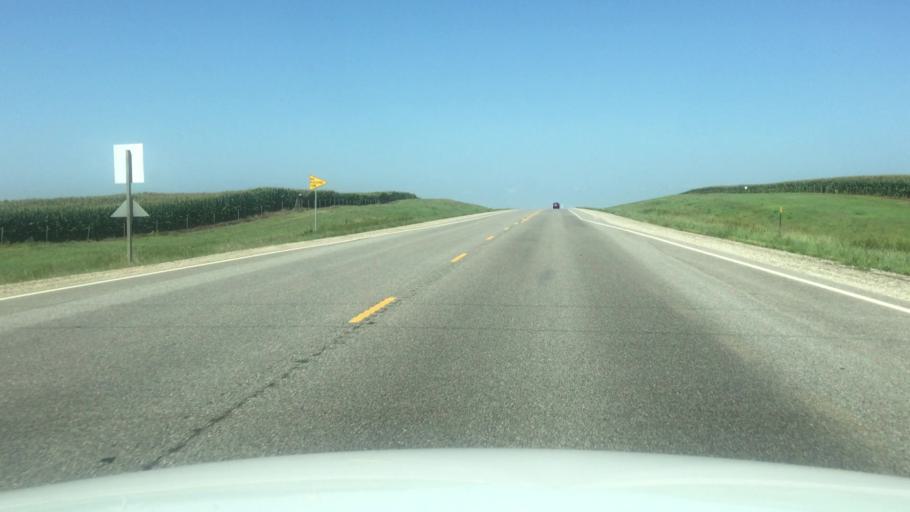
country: US
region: Kansas
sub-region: Doniphan County
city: Highland
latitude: 39.8422
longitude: -95.2844
